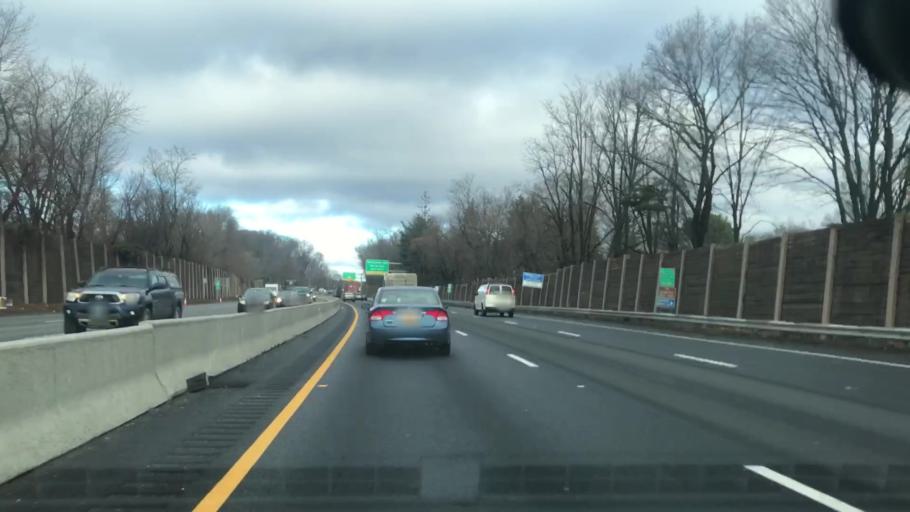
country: US
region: New Jersey
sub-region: Bergen County
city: Ho-Ho-Kus
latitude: 40.9964
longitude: -74.0978
